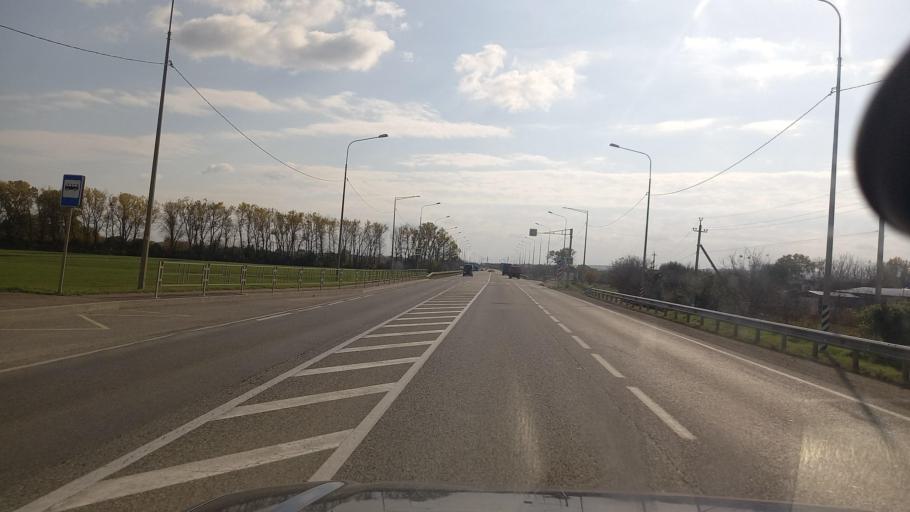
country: RU
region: Krasnodarskiy
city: Novoukrainskiy
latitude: 44.9029
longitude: 38.0337
